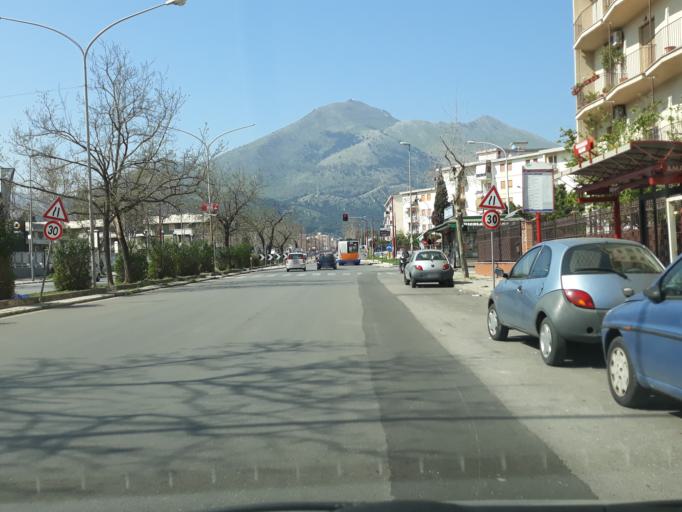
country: IT
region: Sicily
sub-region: Palermo
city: Palermo
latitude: 38.1340
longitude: 13.3112
